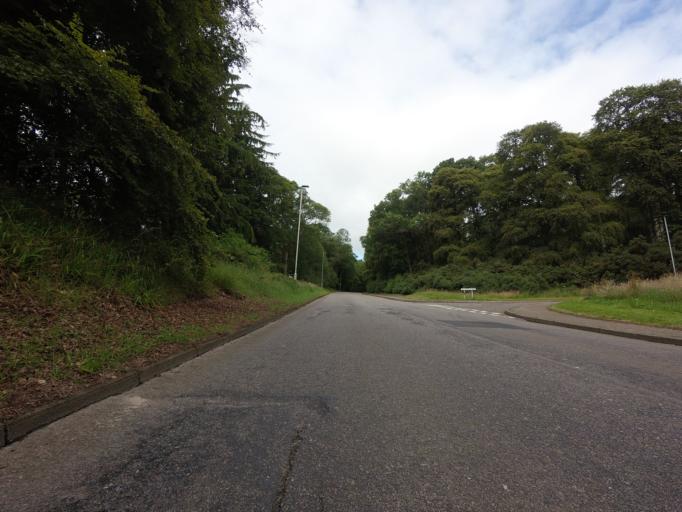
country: GB
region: Scotland
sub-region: Moray
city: Elgin
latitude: 57.6530
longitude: -3.3420
